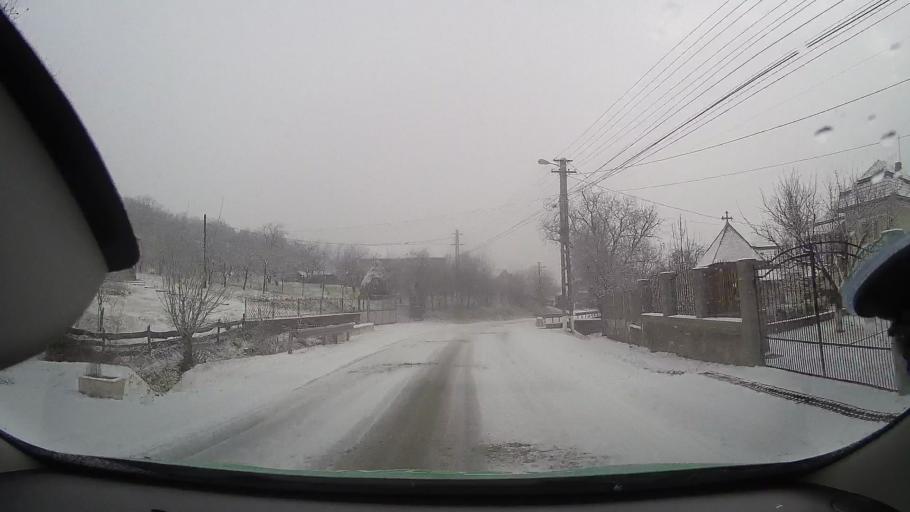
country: RO
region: Alba
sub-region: Comuna Livezile
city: Livezile
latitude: 46.3454
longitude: 23.6543
